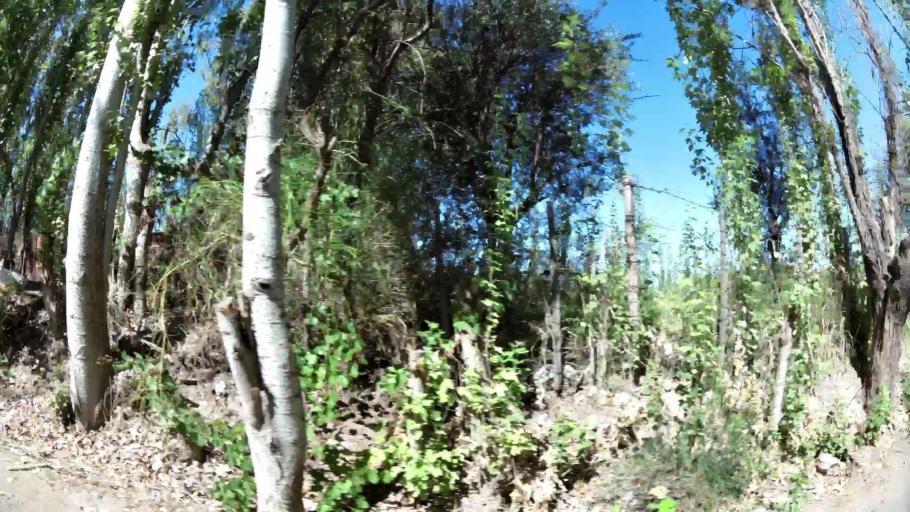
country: AR
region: Mendoza
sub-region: Departamento de Godoy Cruz
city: Godoy Cruz
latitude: -32.9778
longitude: -68.8416
